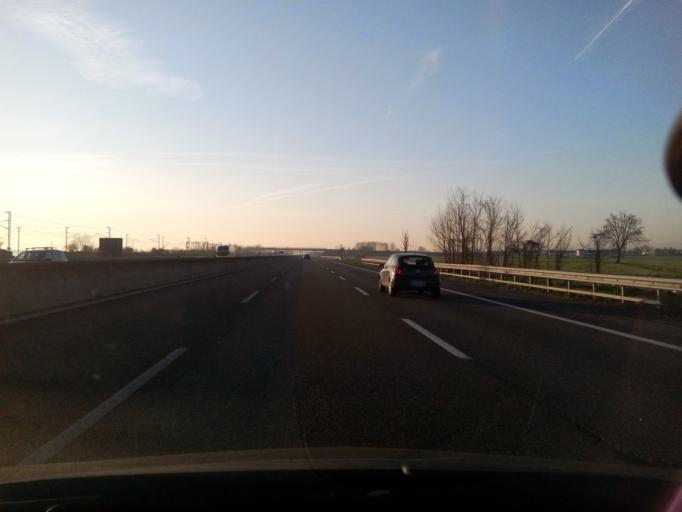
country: IT
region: Lombardy
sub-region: Provincia di Lodi
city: Livraga
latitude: 45.2034
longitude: 9.5454
